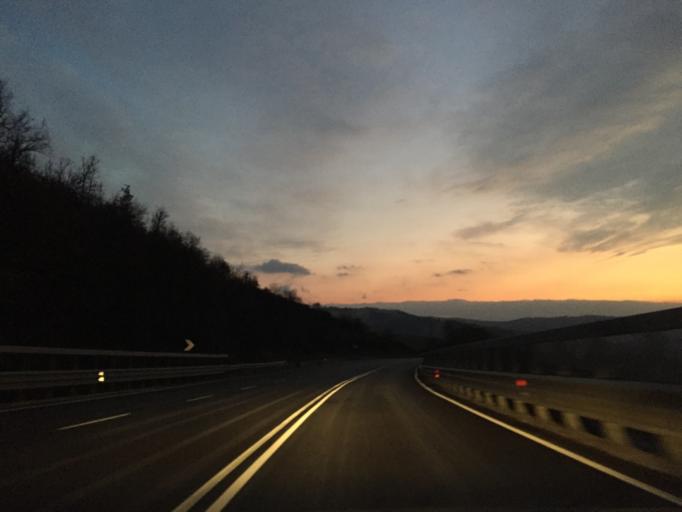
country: IT
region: Apulia
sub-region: Provincia di Foggia
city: Volturino
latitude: 41.4598
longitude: 15.0924
